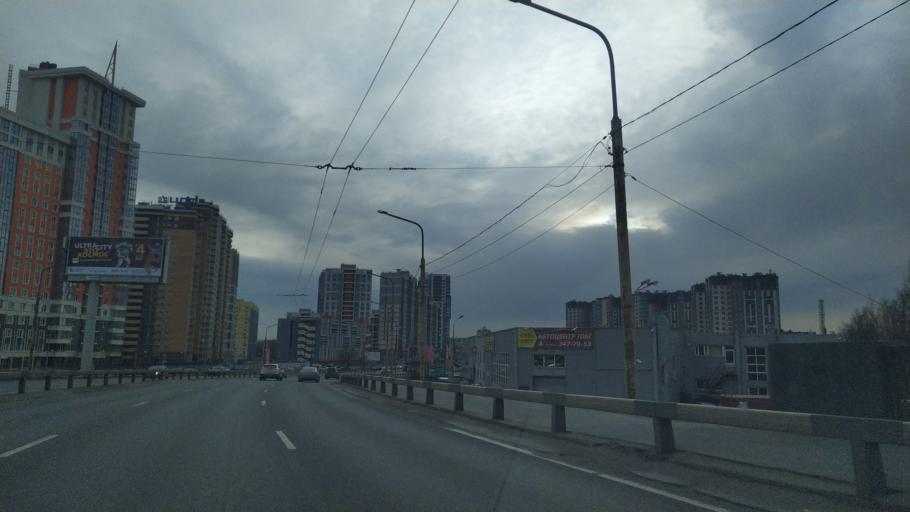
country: RU
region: St.-Petersburg
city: Kushelevka
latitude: 59.9911
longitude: 30.3755
